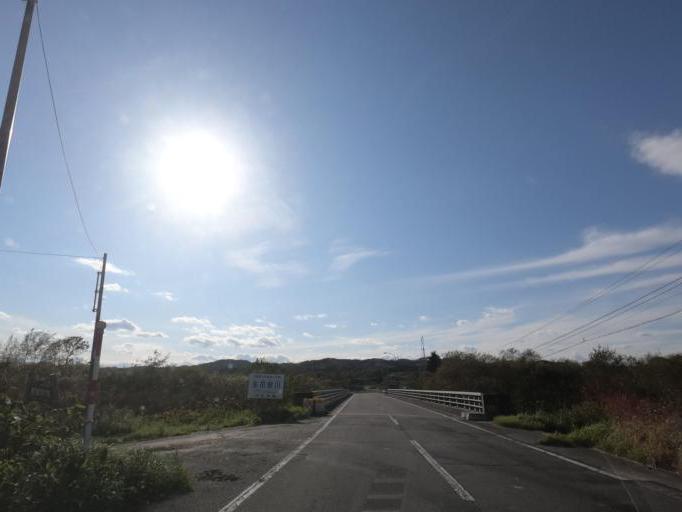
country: JP
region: Hokkaido
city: Obihiro
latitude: 42.6004
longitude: 143.4547
